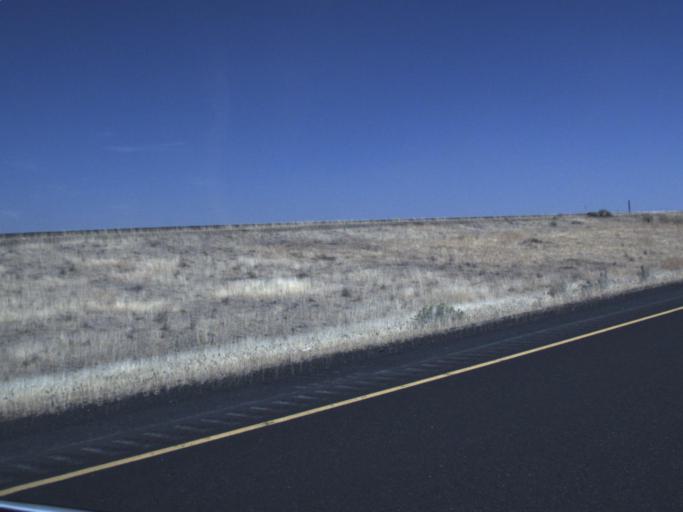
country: US
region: Washington
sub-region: Grant County
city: Warden
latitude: 47.0861
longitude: -118.7250
